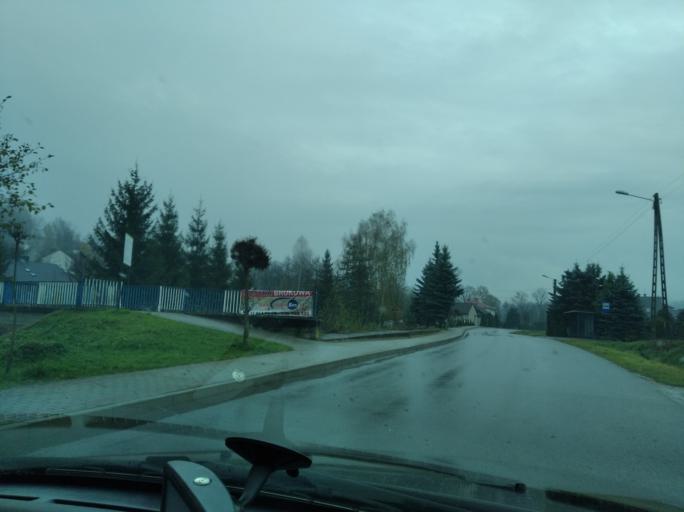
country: PL
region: Subcarpathian Voivodeship
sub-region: Powiat rzeszowski
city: Lubenia
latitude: 49.9289
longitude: 21.9242
